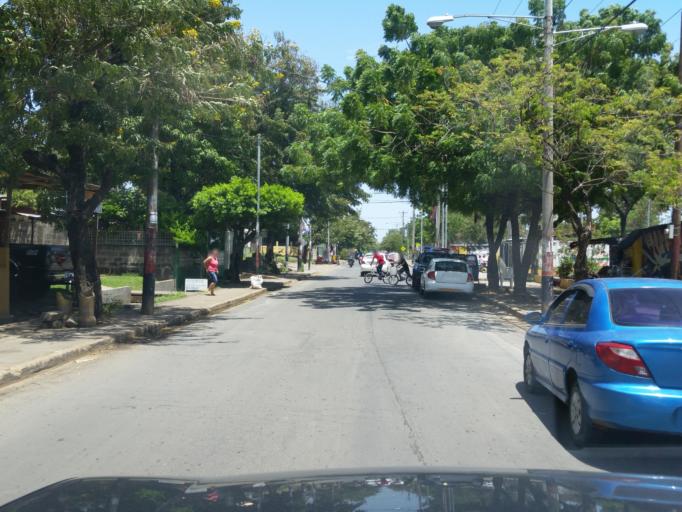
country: NI
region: Managua
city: Managua
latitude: 12.1236
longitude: -86.2128
